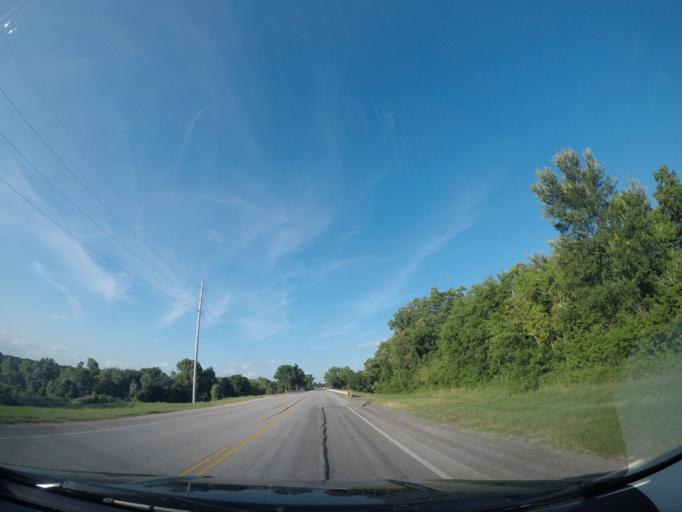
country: US
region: Texas
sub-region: Austin County
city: Wallis
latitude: 29.6700
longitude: -96.0238
